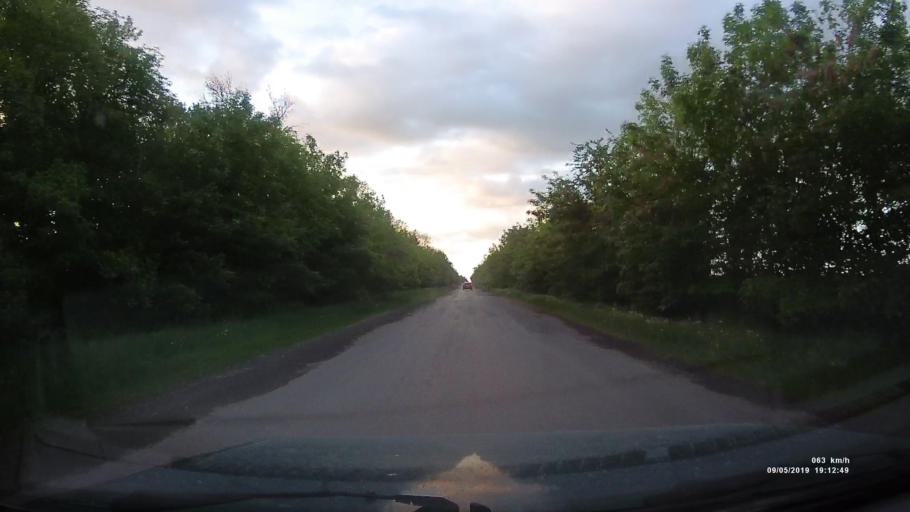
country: RU
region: Krasnodarskiy
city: Kanelovskaya
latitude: 46.7450
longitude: 39.2137
